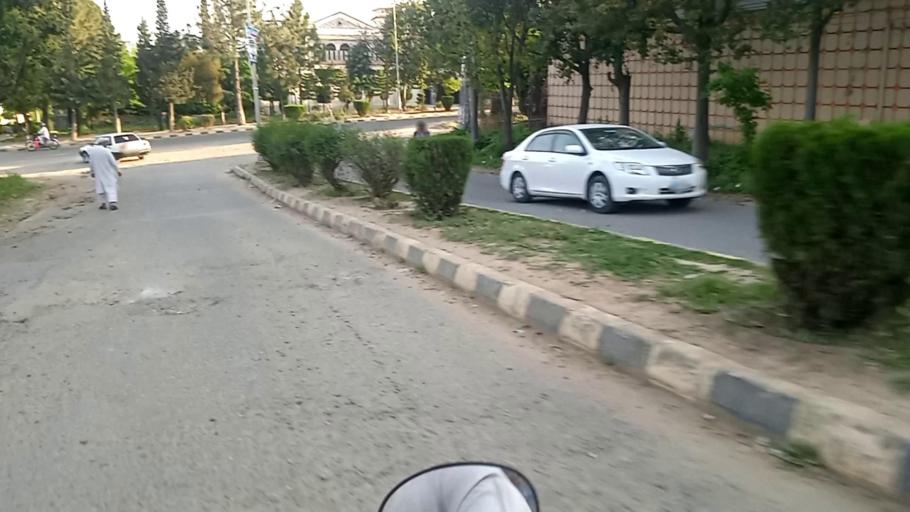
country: PK
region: Khyber Pakhtunkhwa
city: Mingora
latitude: 34.8302
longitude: 72.3426
